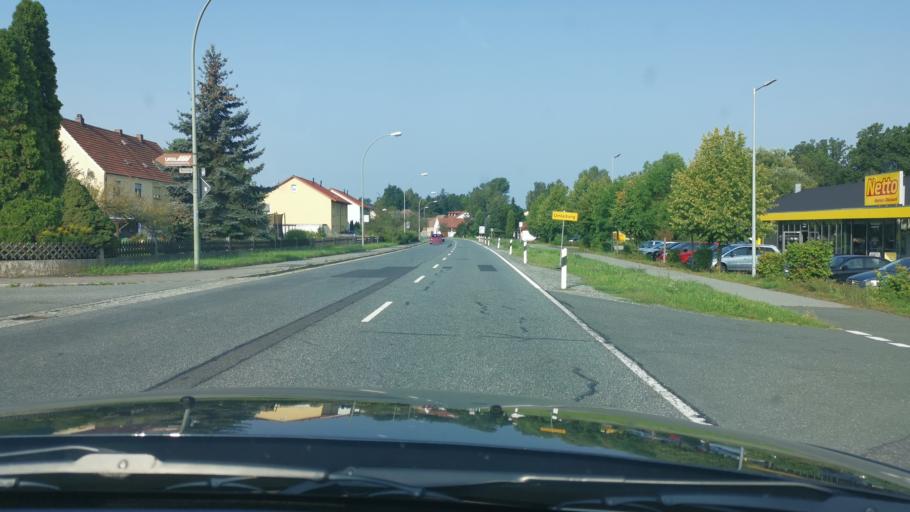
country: DE
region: Bavaria
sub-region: Upper Palatinate
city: Schnaittenbach
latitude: 49.5498
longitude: 12.0117
